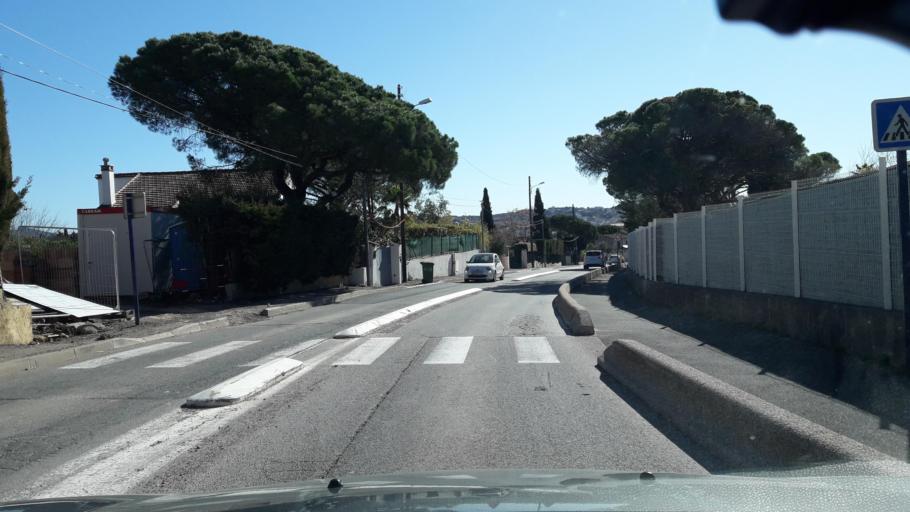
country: FR
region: Provence-Alpes-Cote d'Azur
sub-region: Departement du Var
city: Frejus
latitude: 43.4410
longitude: 6.7550
